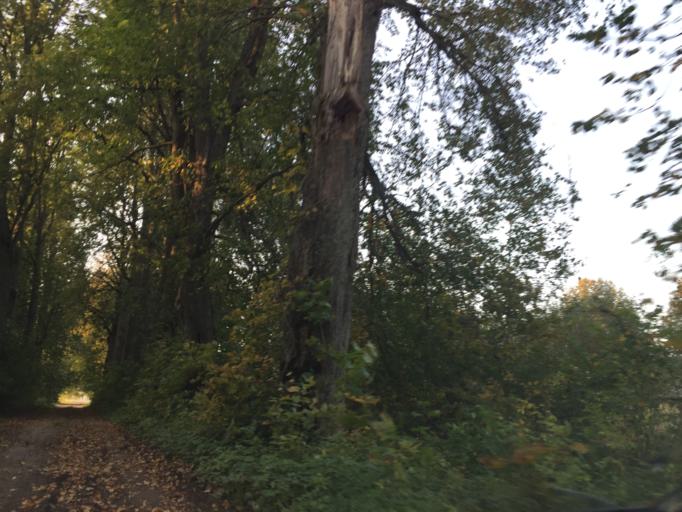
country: LV
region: Lielvarde
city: Lielvarde
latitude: 56.7932
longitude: 24.8241
